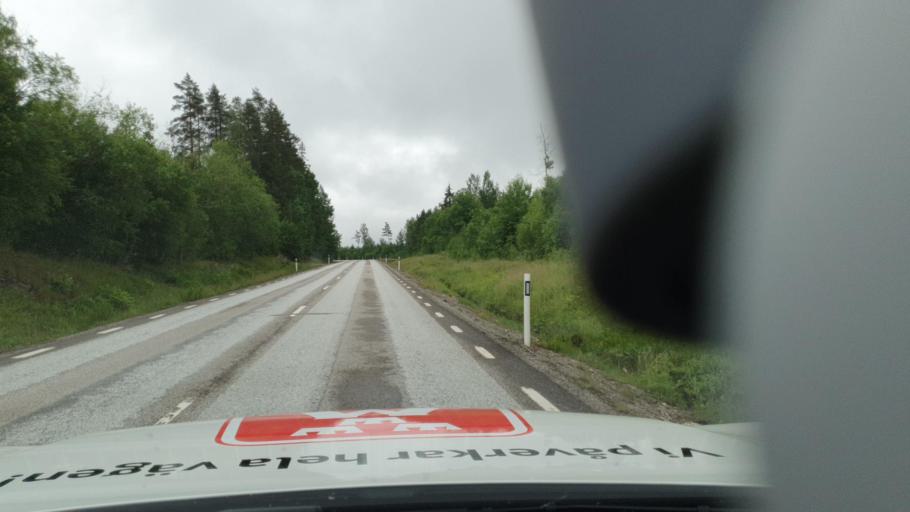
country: SE
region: Vaermland
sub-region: Kristinehamns Kommun
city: Bjorneborg
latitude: 59.2442
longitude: 14.2167
